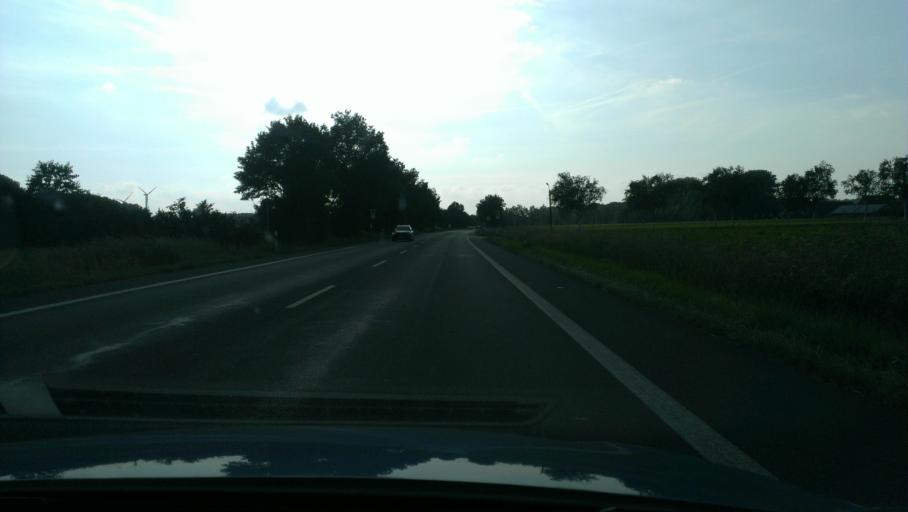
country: DE
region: North Rhine-Westphalia
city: Ahlen
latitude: 51.8200
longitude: 7.9131
